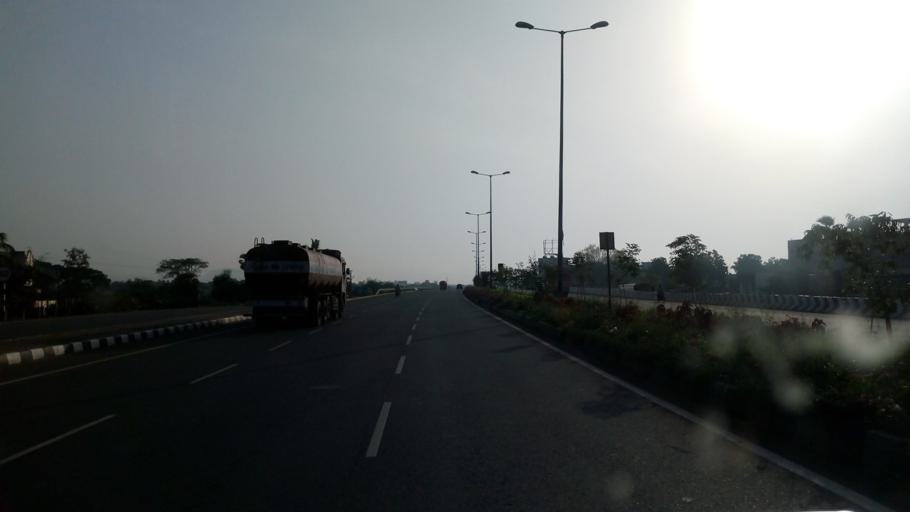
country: IN
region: Andhra Pradesh
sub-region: Guntur
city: Mangalagiri
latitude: 16.3893
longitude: 80.5372
